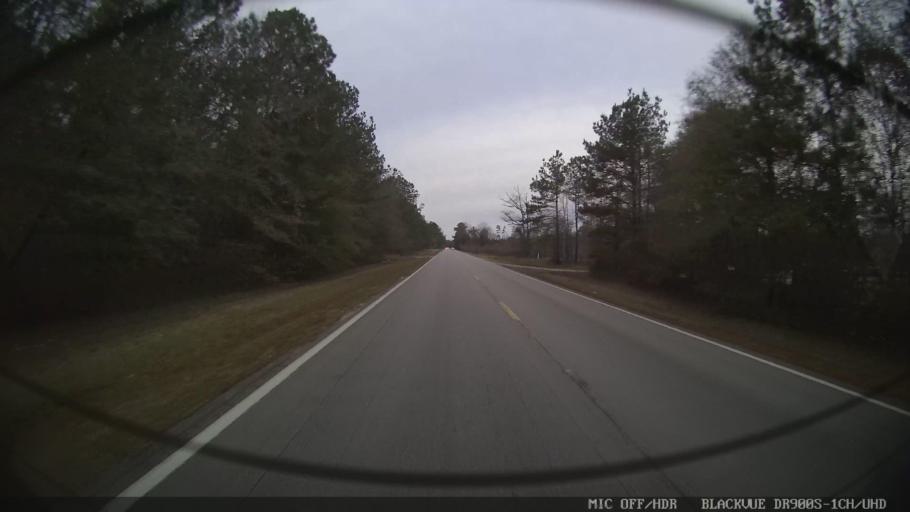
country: US
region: Mississippi
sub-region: Clarke County
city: Stonewall
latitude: 32.0333
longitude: -88.8710
